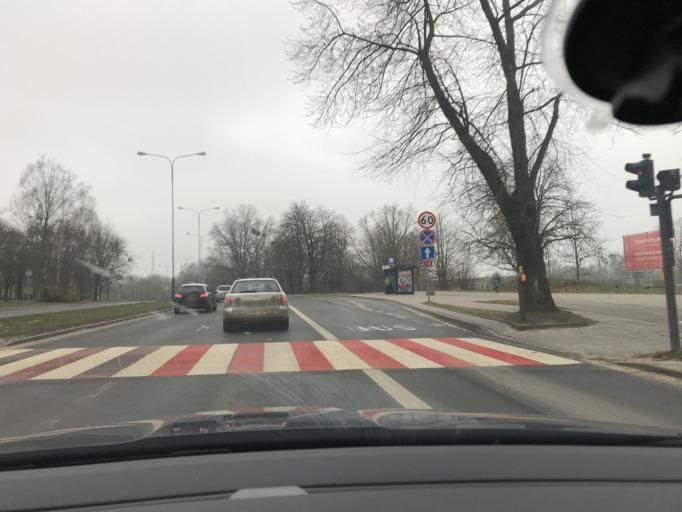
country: PL
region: Lodz Voivodeship
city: Lodz
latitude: 51.7877
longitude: 19.4844
